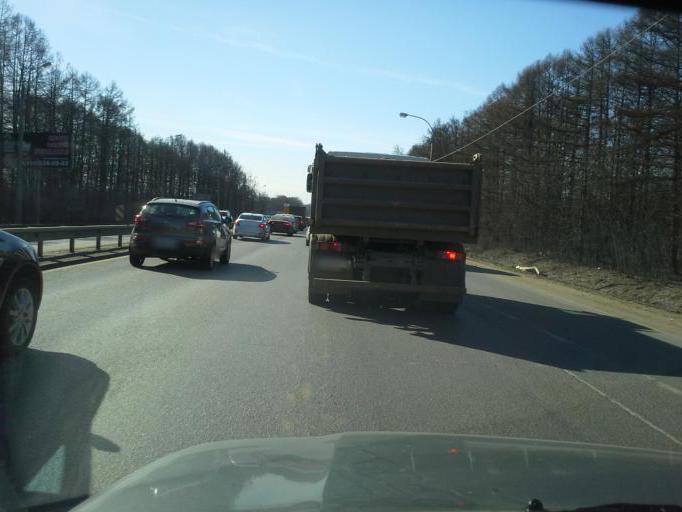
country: RU
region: Moskovskaya
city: Novoivanovskoye
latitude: 55.6903
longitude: 37.3335
